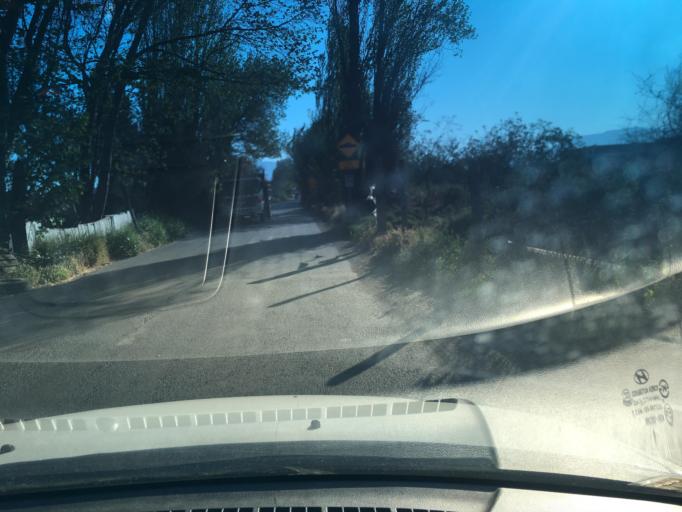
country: CL
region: Santiago Metropolitan
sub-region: Provincia de Chacabuco
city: Chicureo Abajo
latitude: -33.3109
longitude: -70.7162
